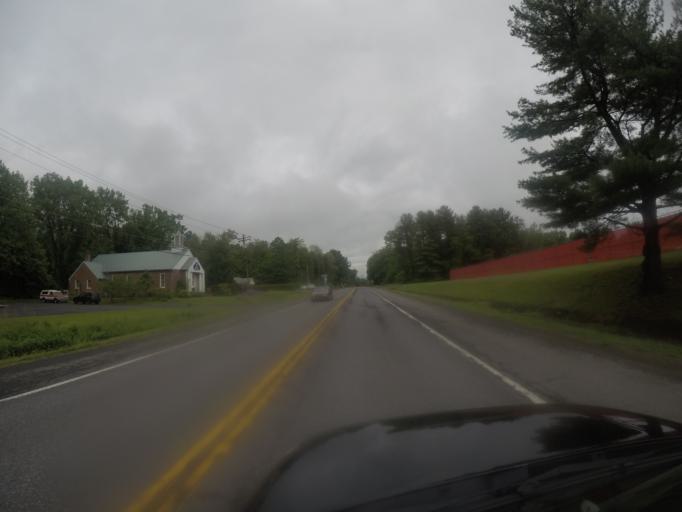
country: US
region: New York
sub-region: Ulster County
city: Shokan
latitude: 42.0100
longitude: -74.2684
